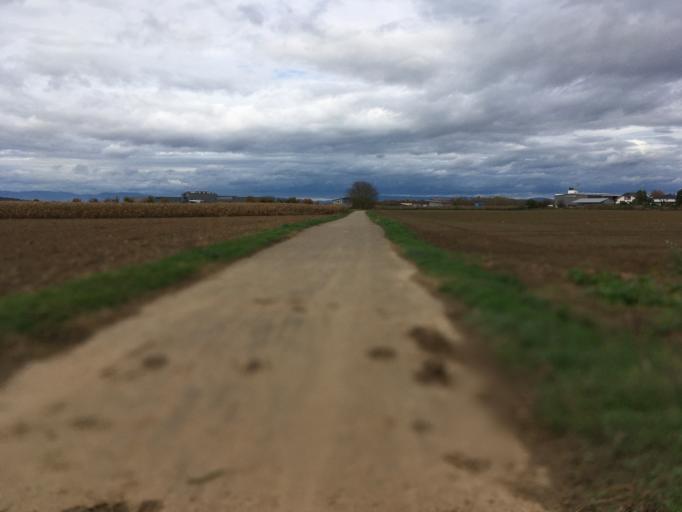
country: DE
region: Baden-Wuerttemberg
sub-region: Freiburg Region
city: Endingen
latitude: 48.1460
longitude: 7.6921
